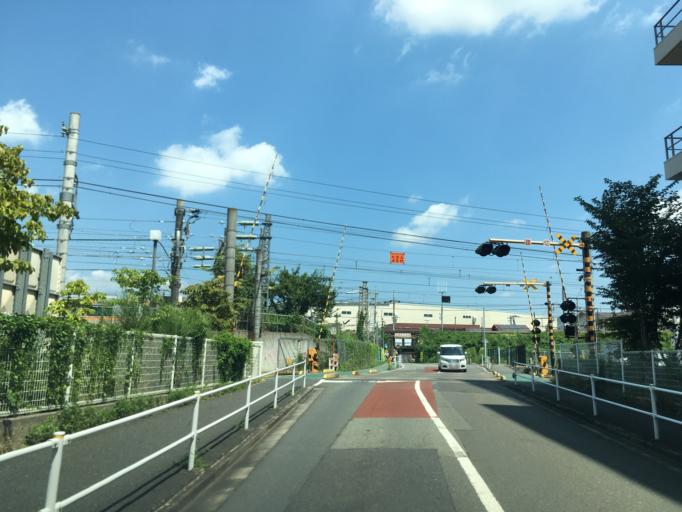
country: JP
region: Tokyo
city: Fussa
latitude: 35.7166
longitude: 139.3500
